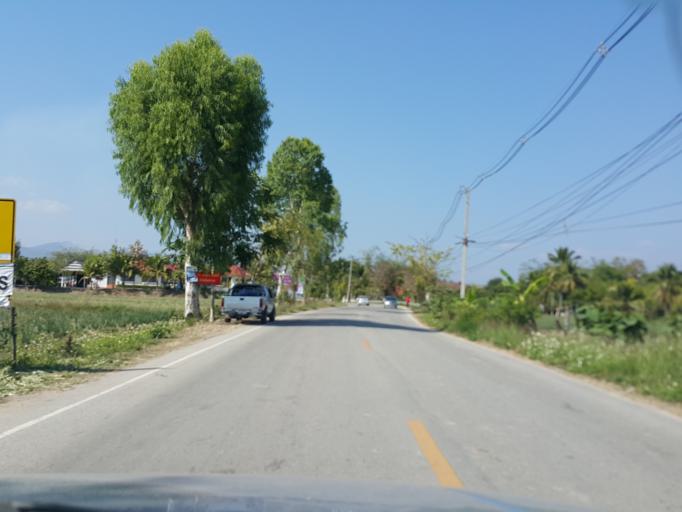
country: TH
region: Chiang Mai
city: Mae Wang
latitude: 18.6026
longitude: 98.7991
